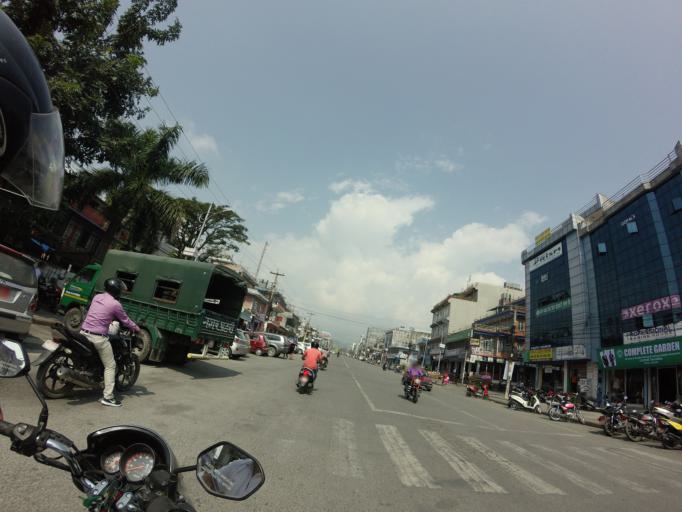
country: NP
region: Western Region
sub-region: Gandaki Zone
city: Pokhara
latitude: 28.2176
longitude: 83.9864
